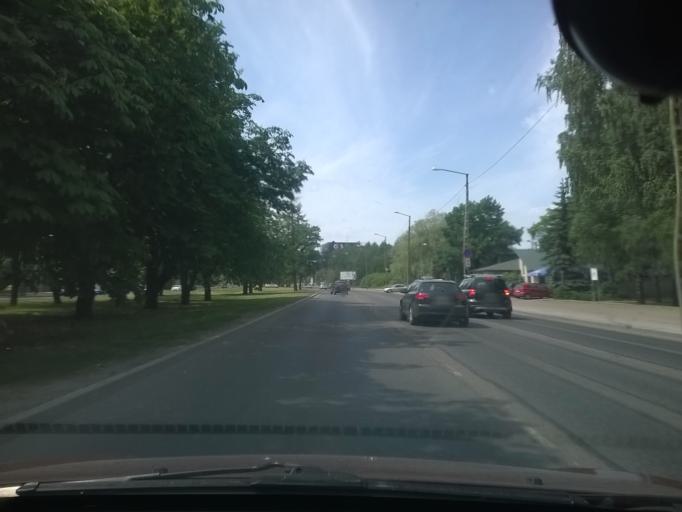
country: EE
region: Harju
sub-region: Tallinna linn
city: Tallinn
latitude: 59.4298
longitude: 24.6912
